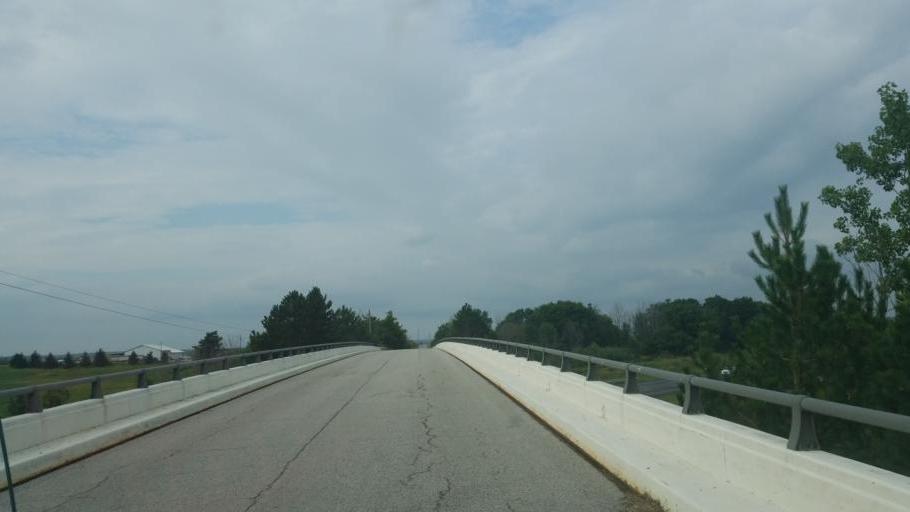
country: US
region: Ohio
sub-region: Wayne County
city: West Salem
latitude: 40.9672
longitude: -82.0538
